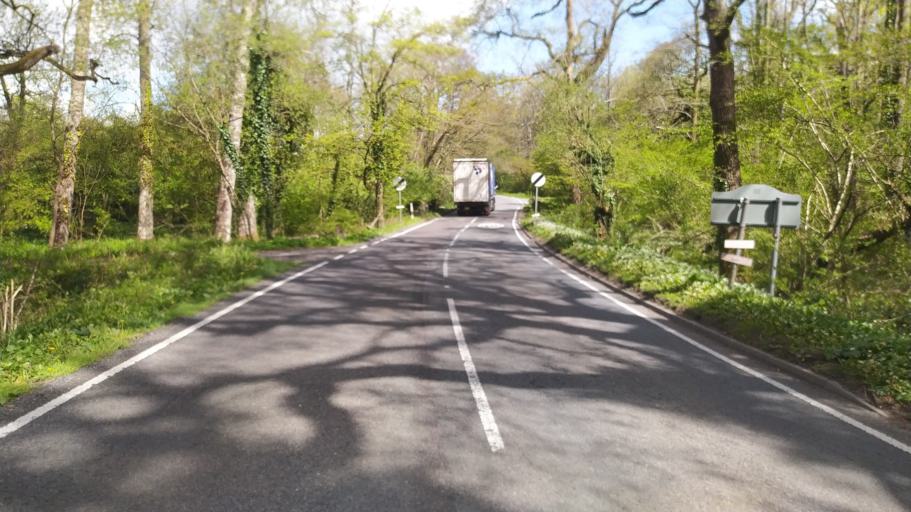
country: GB
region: England
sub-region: Wiltshire
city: Kilmington
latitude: 51.1737
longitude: -2.3009
